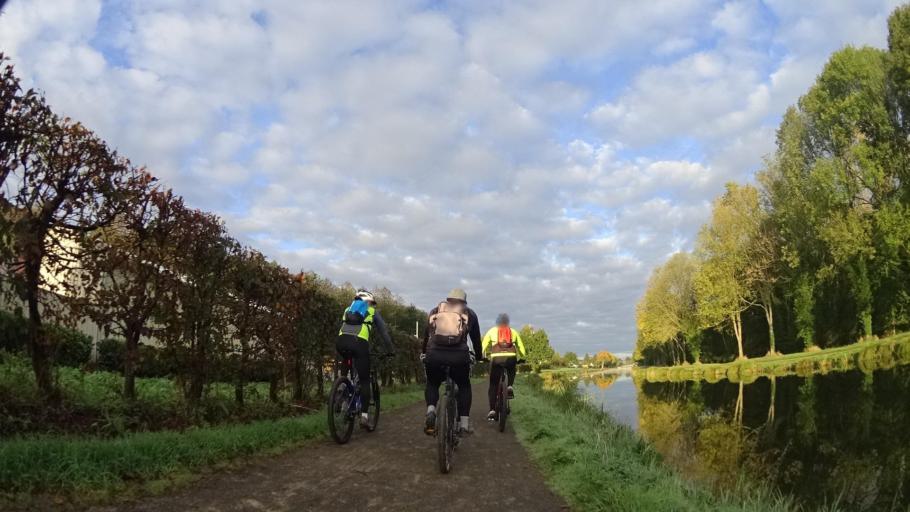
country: FR
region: Brittany
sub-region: Departement des Cotes-d'Armor
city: Evran
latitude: 48.3815
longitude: -1.9730
